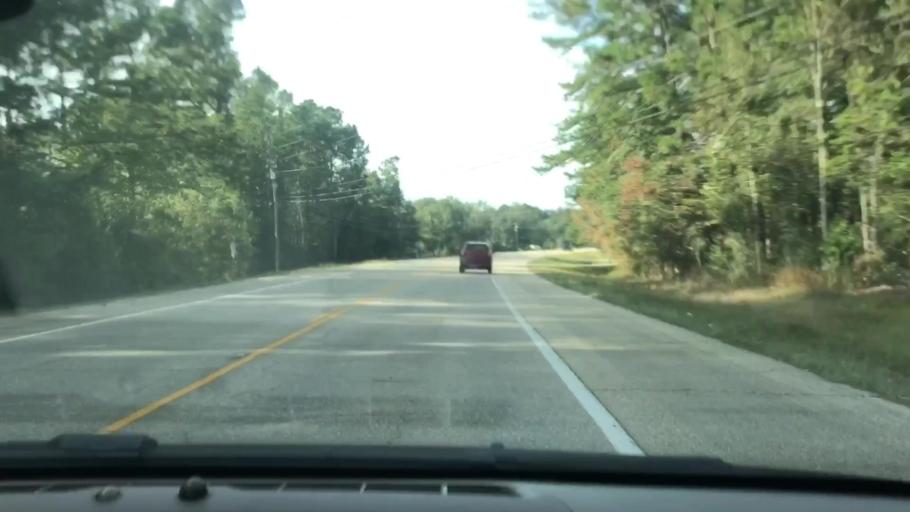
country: US
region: Louisiana
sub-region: Saint Tammany Parish
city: Pearl River
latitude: 30.4447
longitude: -89.7960
